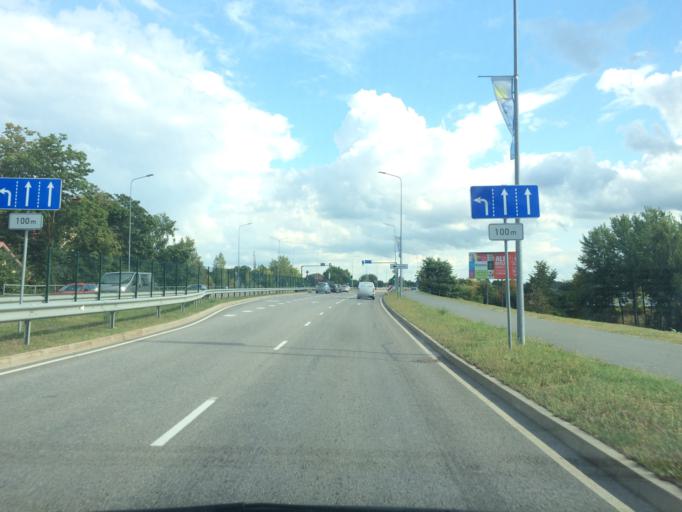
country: LV
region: Ogre
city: Ogre
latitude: 56.8125
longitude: 24.5977
